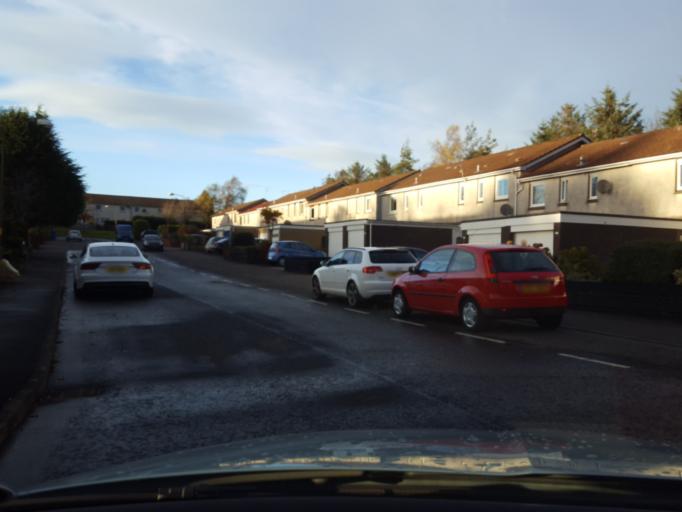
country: GB
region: Scotland
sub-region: West Lothian
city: Livingston
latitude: 55.9061
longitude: -3.5364
